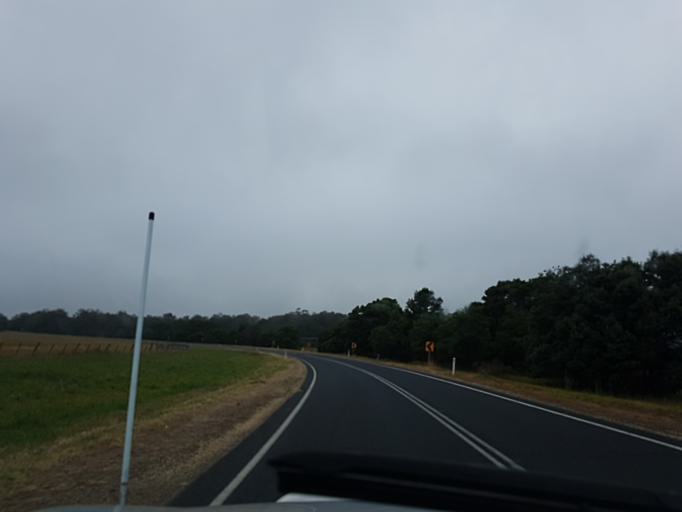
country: AU
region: Victoria
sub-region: Wellington
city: Sale
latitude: -38.0863
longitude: 147.0075
